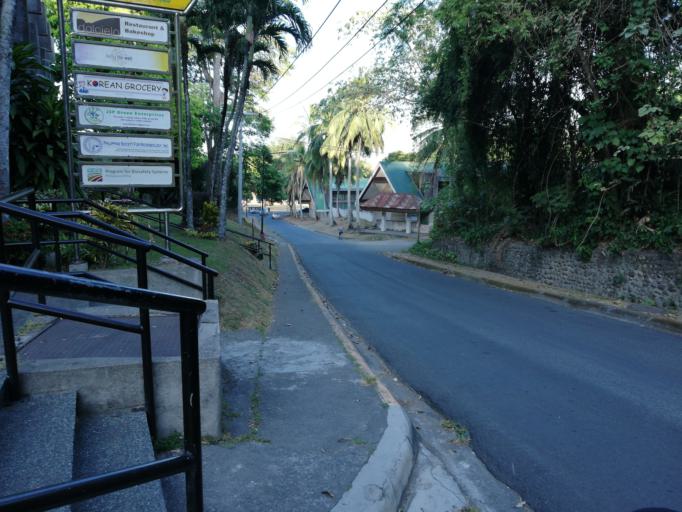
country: PH
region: Calabarzon
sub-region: Province of Laguna
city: Los Banos
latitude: 14.1614
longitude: 121.2396
